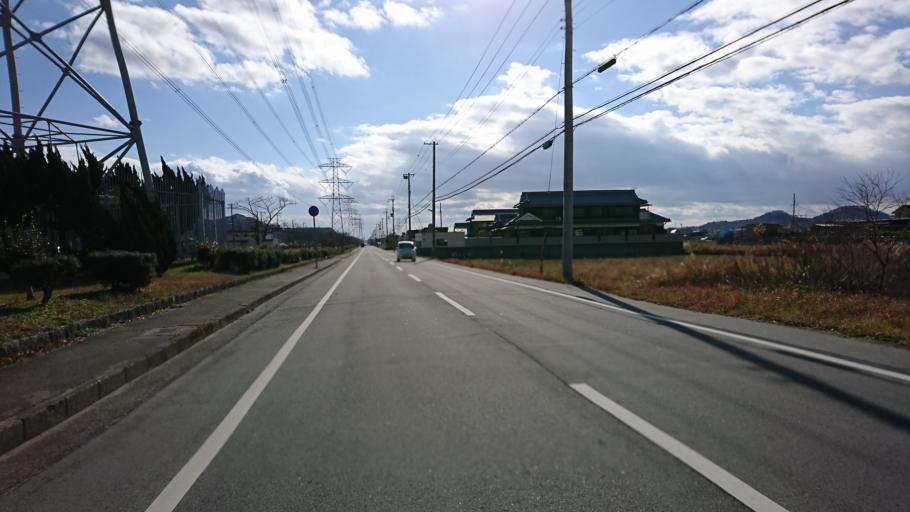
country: JP
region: Hyogo
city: Kakogawacho-honmachi
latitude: 34.8023
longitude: 134.7829
